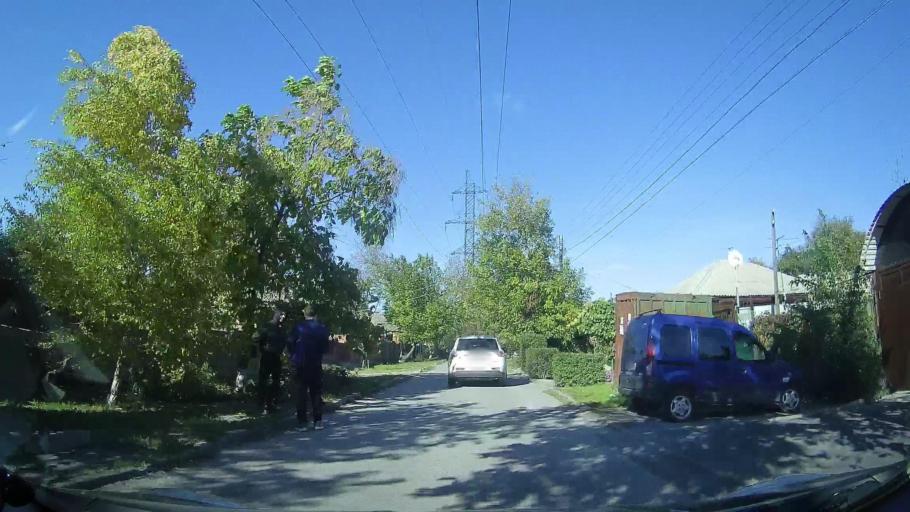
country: RU
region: Rostov
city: Rostov-na-Donu
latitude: 47.2393
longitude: 39.6726
